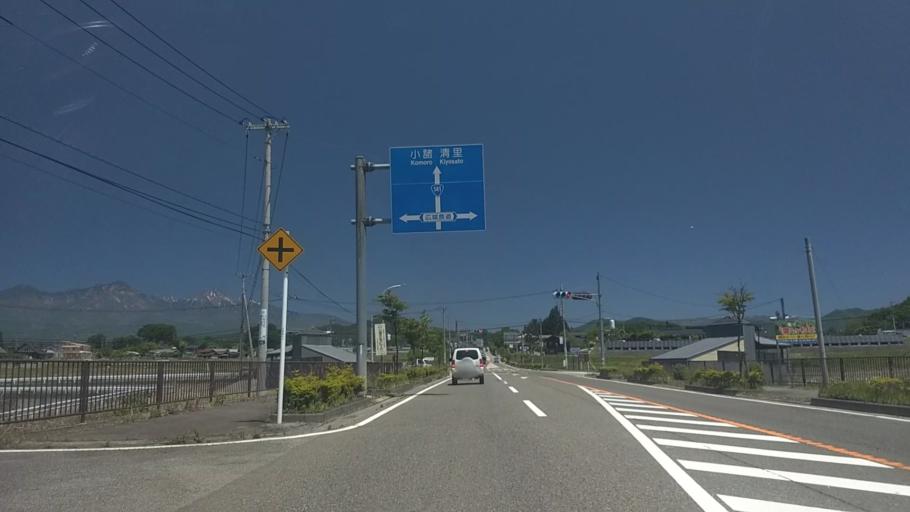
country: JP
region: Yamanashi
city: Nirasaki
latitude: 35.8294
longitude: 138.4297
